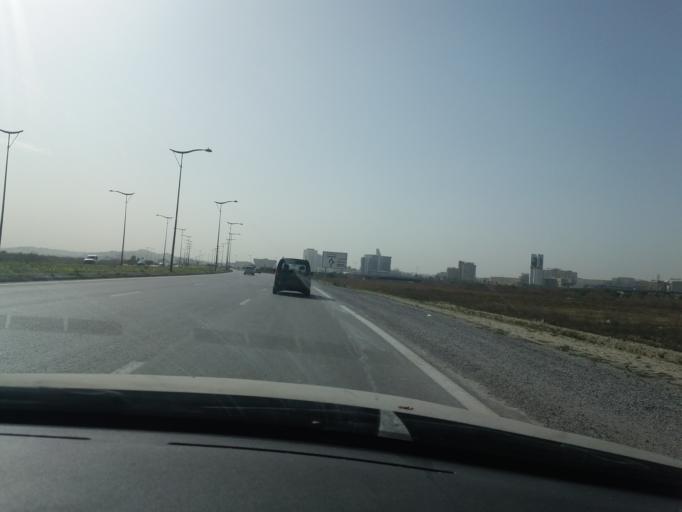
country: TN
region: Tunis
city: Tunis
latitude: 36.8167
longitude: 10.1958
